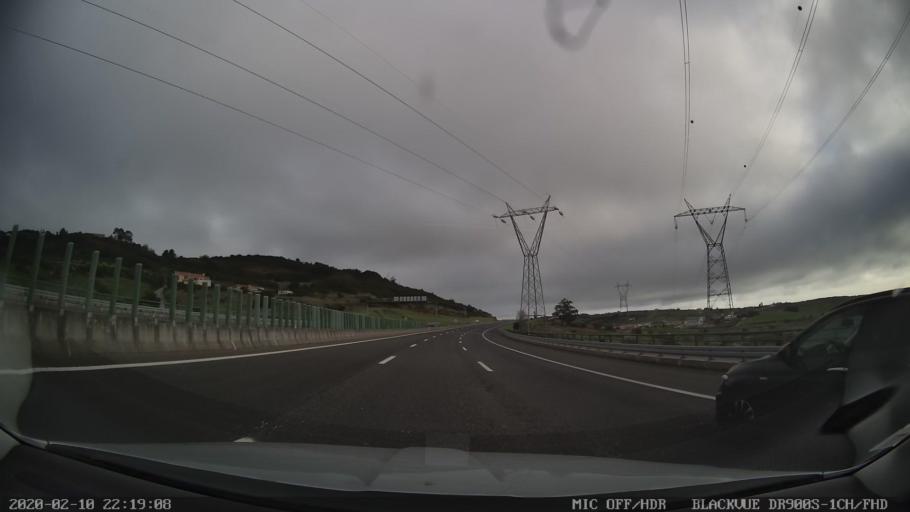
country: PT
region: Lisbon
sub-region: Arruda Dos Vinhos
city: Arruda dos Vinhos
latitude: 38.9511
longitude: -9.0666
